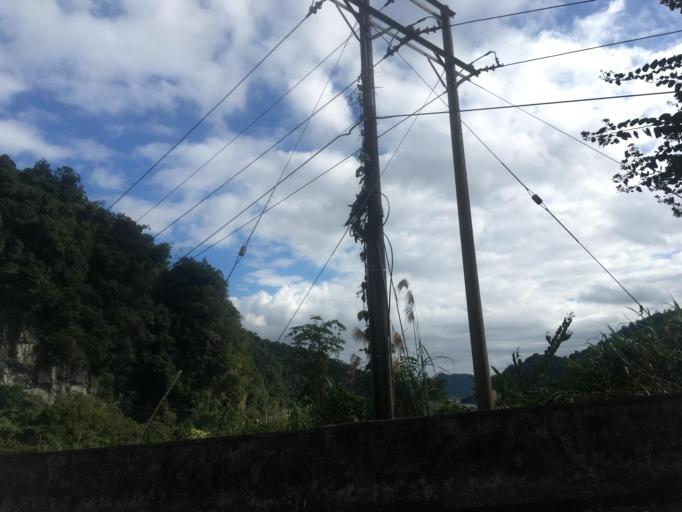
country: TW
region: Taiwan
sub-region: Yilan
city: Yilan
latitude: 24.6373
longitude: 121.5529
